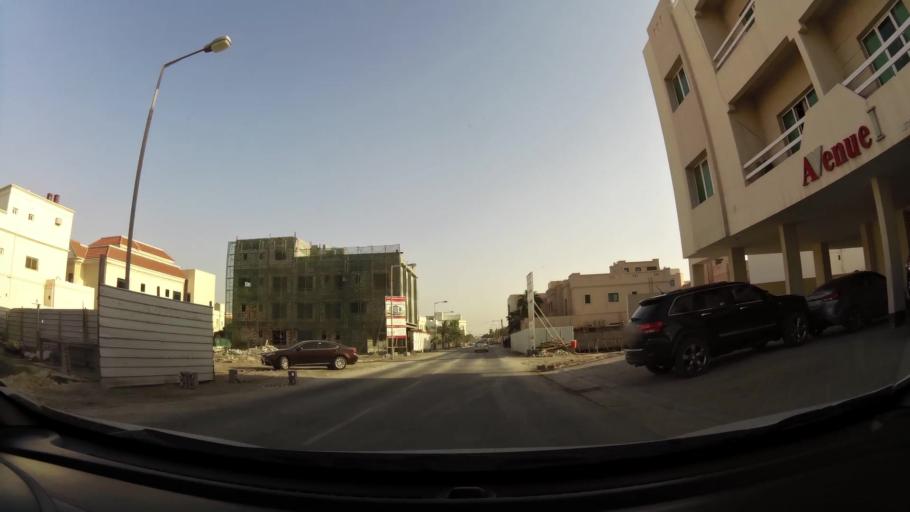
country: BH
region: Manama
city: Jidd Hafs
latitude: 26.2082
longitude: 50.4995
